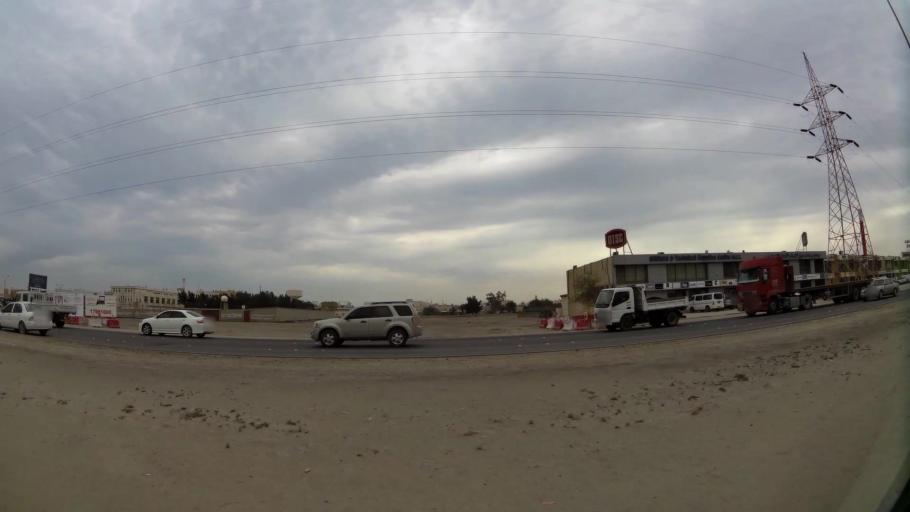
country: BH
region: Northern
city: Sitrah
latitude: 26.1634
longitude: 50.6045
